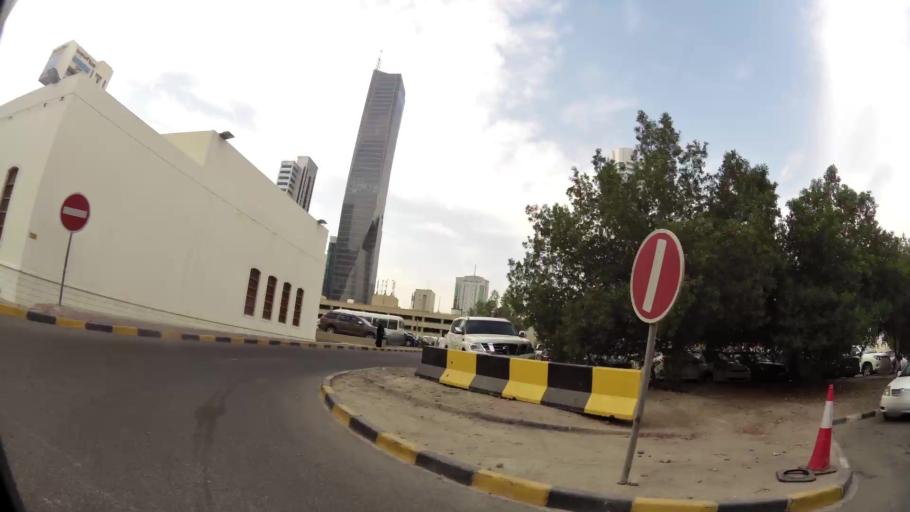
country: KW
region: Al Asimah
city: Kuwait City
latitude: 29.3797
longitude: 47.9790
